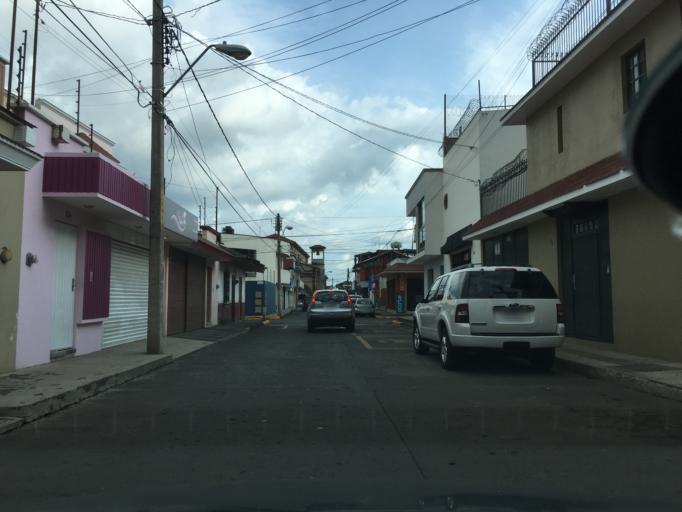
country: MX
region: Michoacan
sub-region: Uruapan
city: Uruapan
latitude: 19.4151
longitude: -102.0556
